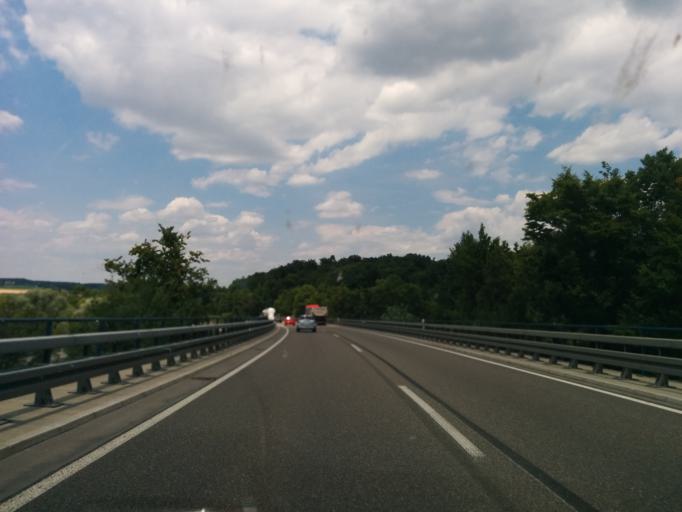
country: DE
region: Bavaria
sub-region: Swabia
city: Donauwoerth
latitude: 48.7277
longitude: 10.7856
